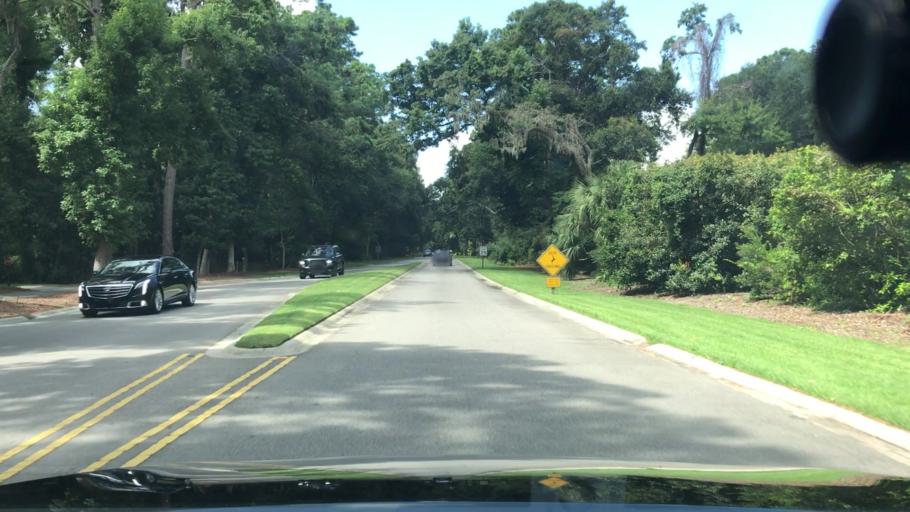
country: US
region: South Carolina
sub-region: Beaufort County
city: Hilton Head Island
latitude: 32.1538
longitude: -80.7699
